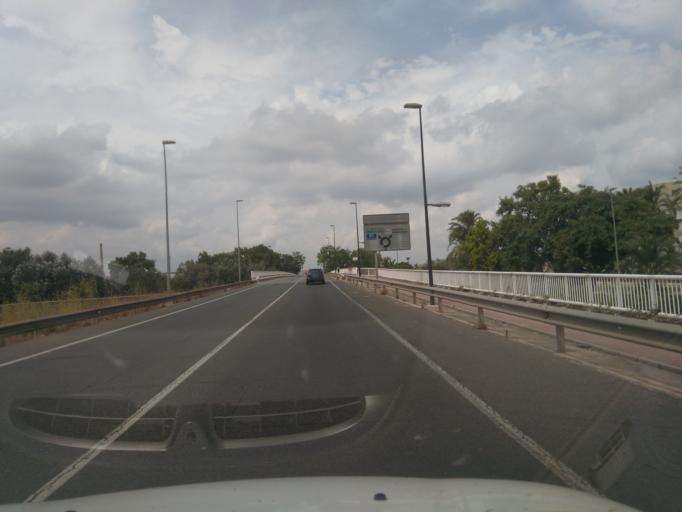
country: ES
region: Valencia
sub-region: Provincia de Valencia
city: Alzira
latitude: 39.1524
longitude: -0.4458
